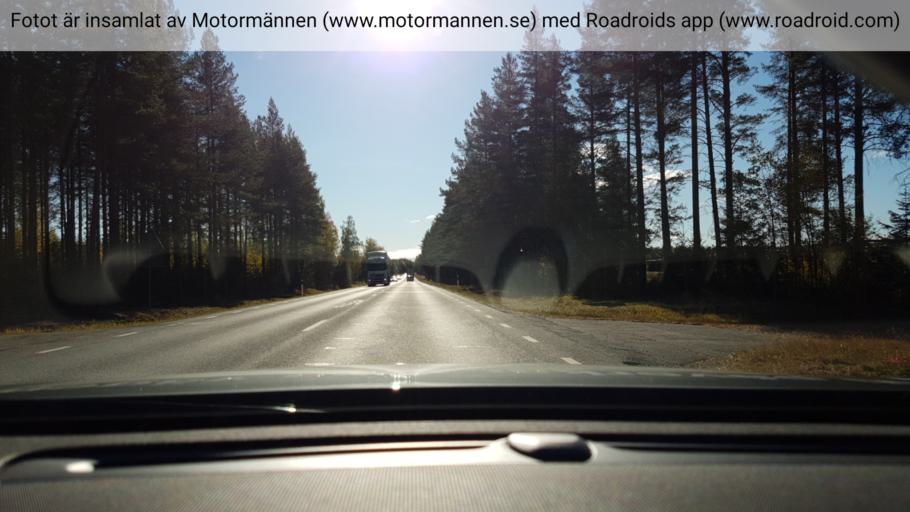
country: SE
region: Vaesterbotten
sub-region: Skelleftea Kommun
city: Burea
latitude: 64.5602
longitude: 21.2361
